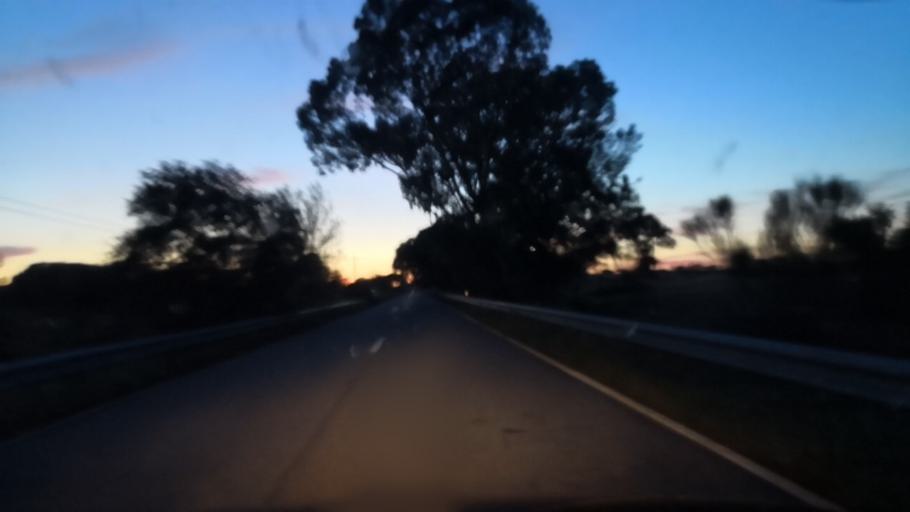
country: ES
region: Extremadura
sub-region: Provincia de Caceres
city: Piedras Albas
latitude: 39.8643
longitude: -7.0125
